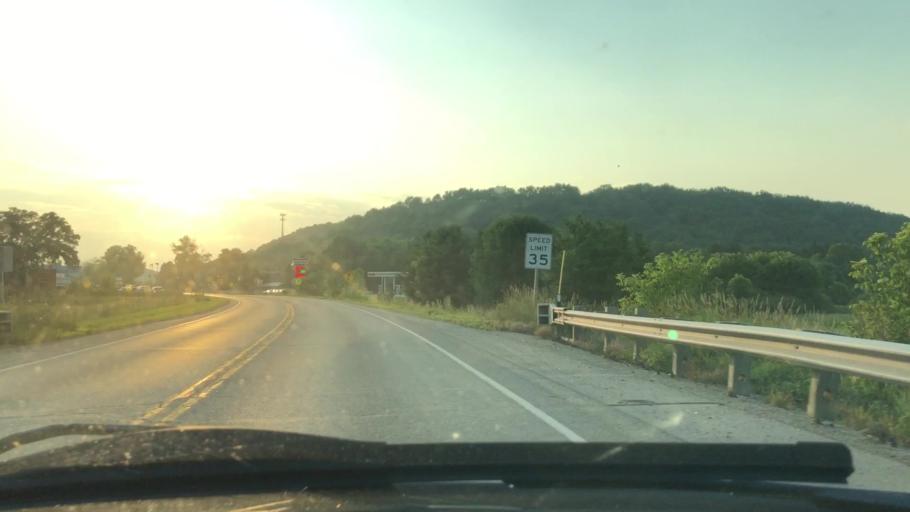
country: US
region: Wisconsin
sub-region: Dane County
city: Black Earth
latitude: 43.1420
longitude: -89.7440
